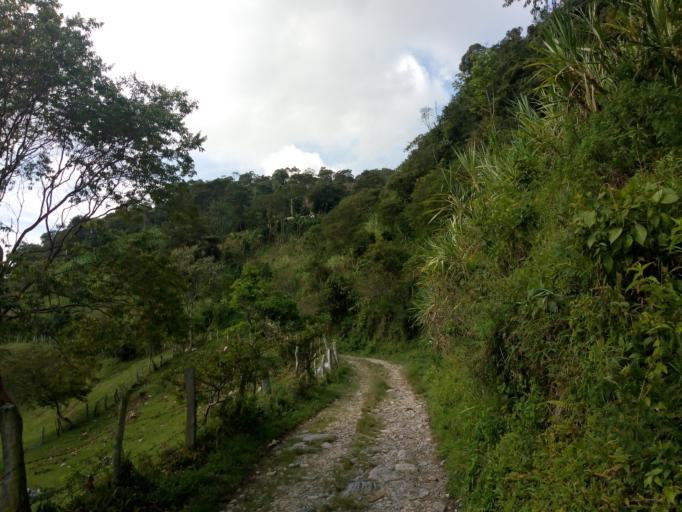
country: CO
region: Boyaca
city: Moniquira
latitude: 5.8730
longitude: -73.5040
